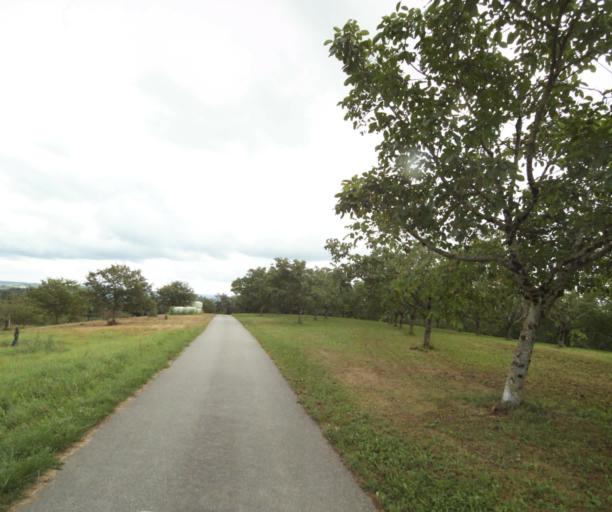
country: FR
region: Limousin
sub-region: Departement de la Correze
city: Sainte-Fortunade
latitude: 45.1726
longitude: 1.8373
